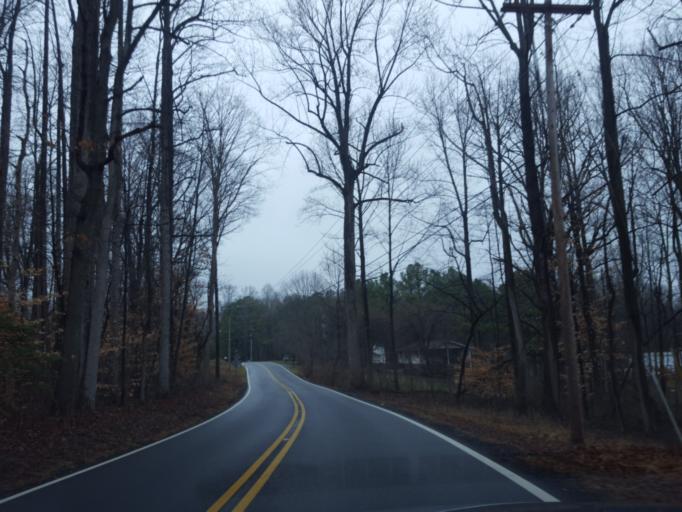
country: US
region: Maryland
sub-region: Calvert County
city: Huntingtown
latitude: 38.6102
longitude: -76.5481
